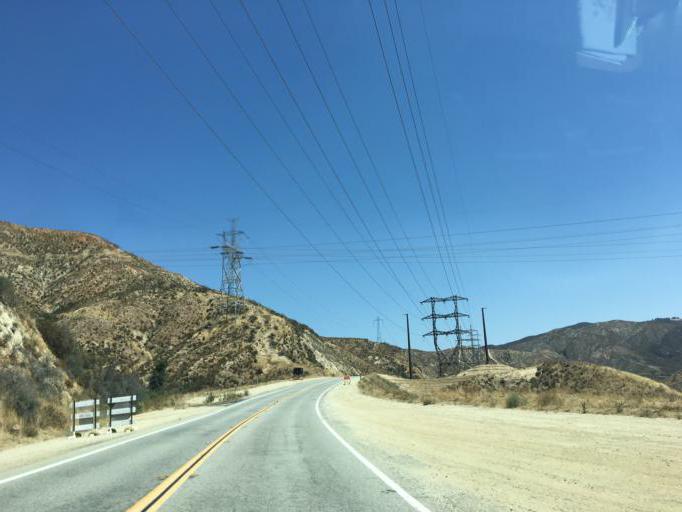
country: US
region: California
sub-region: Los Angeles County
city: Green Valley
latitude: 34.5987
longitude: -118.4485
